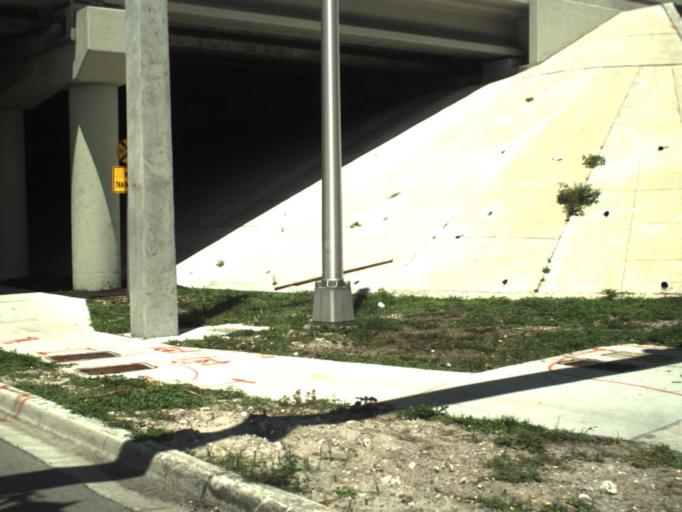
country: US
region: Florida
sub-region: Broward County
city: Hollywood
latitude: 26.0111
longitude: -80.1663
